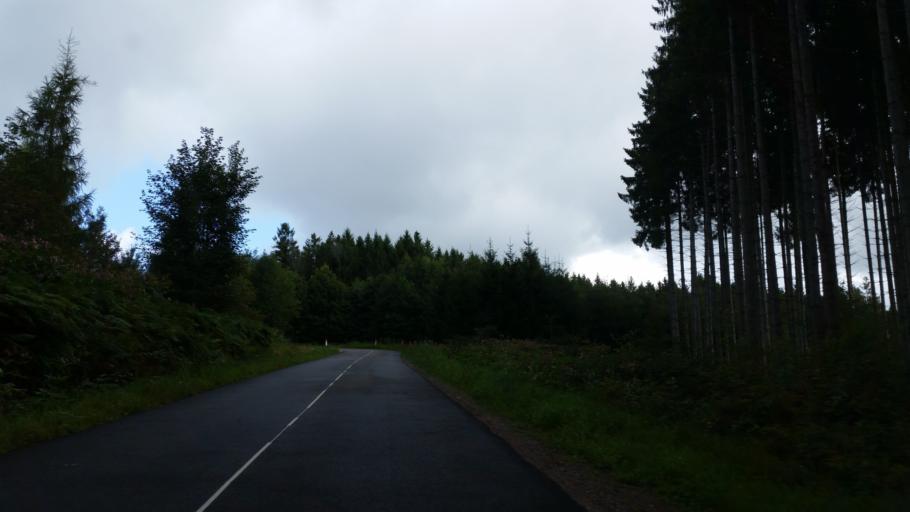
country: FR
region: Lorraine
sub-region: Departement des Vosges
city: Granges-sur-Vologne
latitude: 48.1198
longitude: 6.7804
